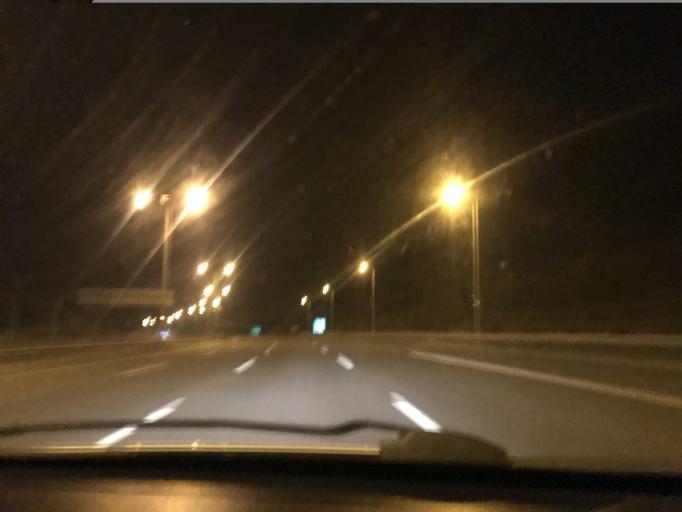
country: TR
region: Ankara
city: Etimesgut
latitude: 39.8539
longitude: 32.6258
